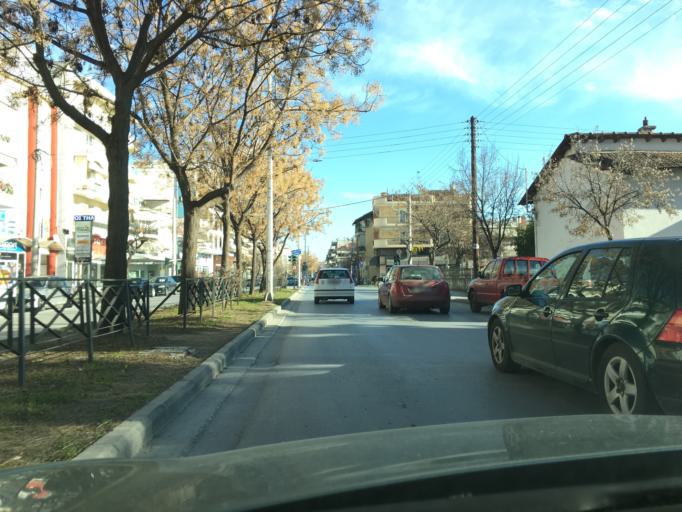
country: GR
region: Thessaly
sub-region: Nomos Larisis
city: Larisa
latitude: 39.6324
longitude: 22.4102
